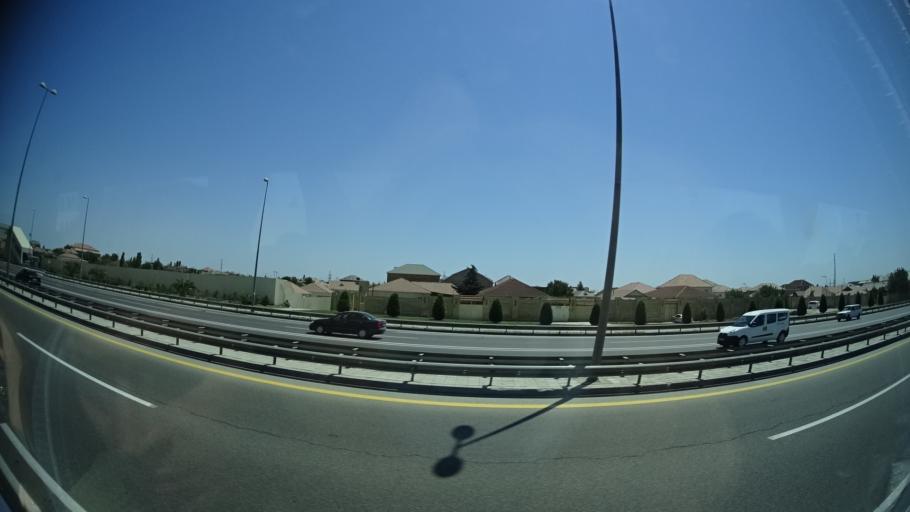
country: AZ
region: Baki
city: Ramana
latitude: 40.4437
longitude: 49.9924
